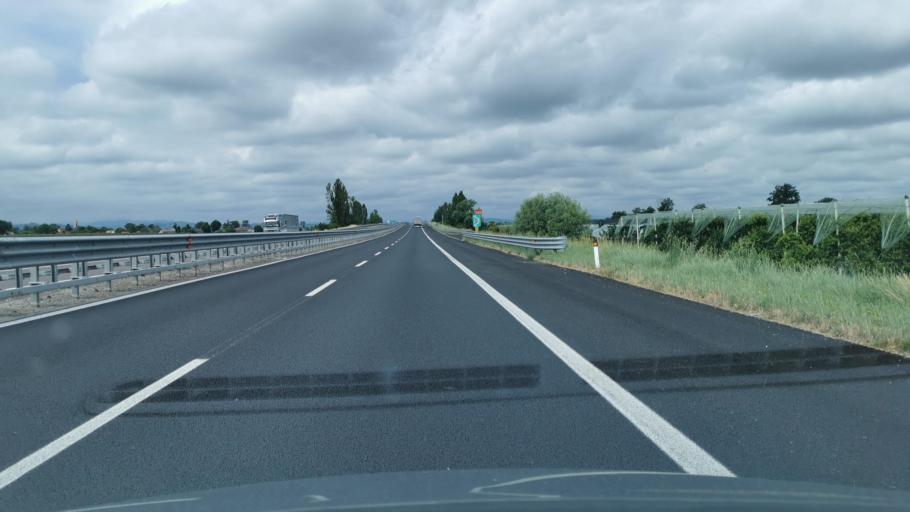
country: IT
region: Emilia-Romagna
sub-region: Provincia di Ravenna
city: Solarolo
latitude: 44.3700
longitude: 11.8472
